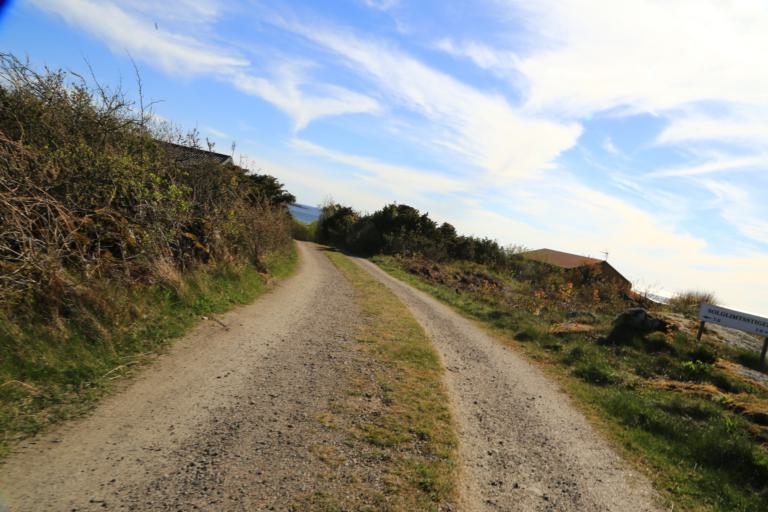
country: SE
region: Halland
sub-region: Varbergs Kommun
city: Varberg
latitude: 57.0871
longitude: 12.2594
